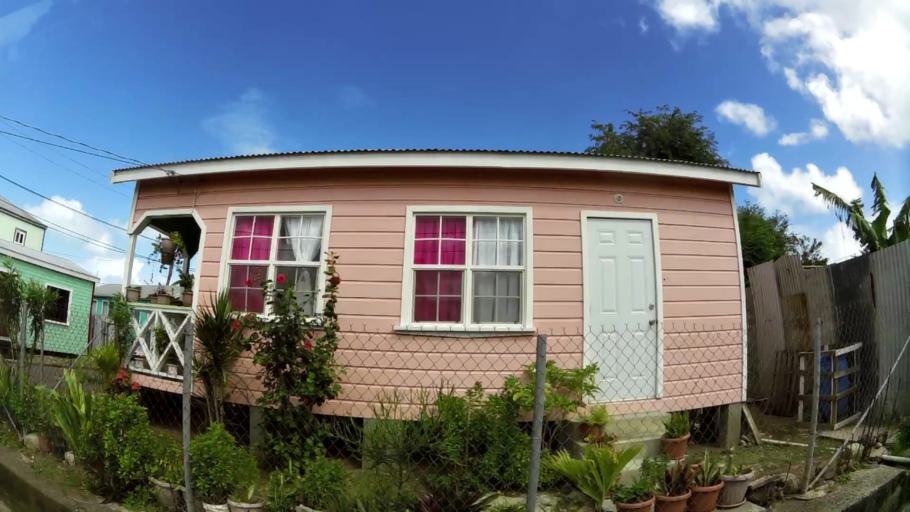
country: AG
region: Saint John
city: Saint John's
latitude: 17.1135
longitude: -61.8426
